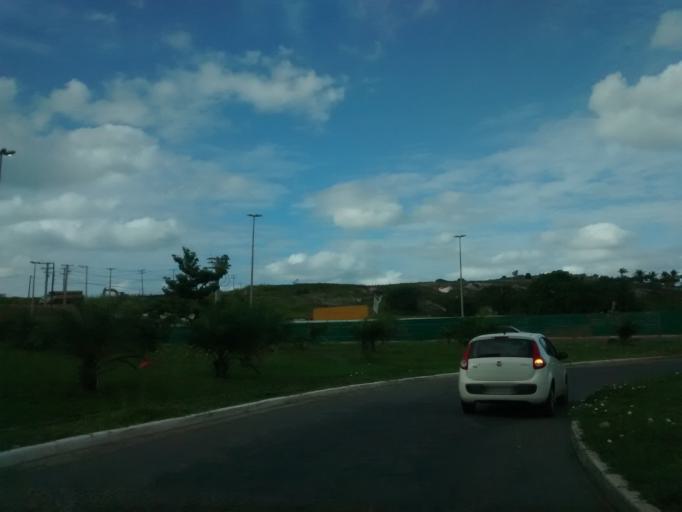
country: BR
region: Bahia
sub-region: Lauro De Freitas
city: Lauro de Freitas
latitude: -12.9207
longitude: -38.3525
